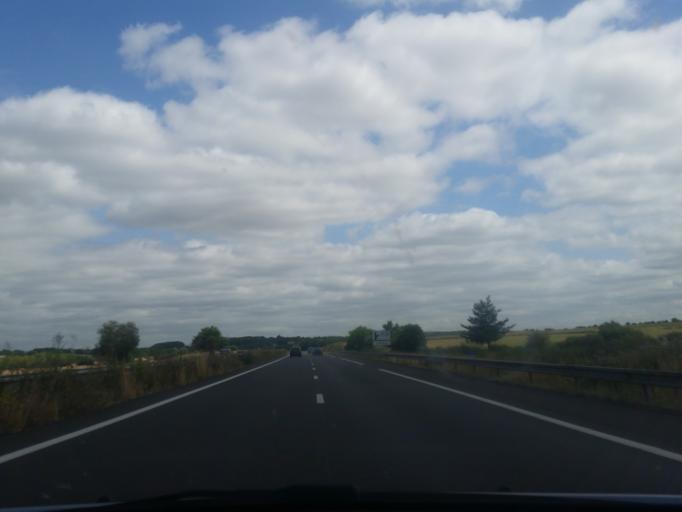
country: FR
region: Pays de la Loire
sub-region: Departement de Maine-et-Loire
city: Saint-Leger-des-Bois
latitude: 47.4495
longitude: -0.7169
